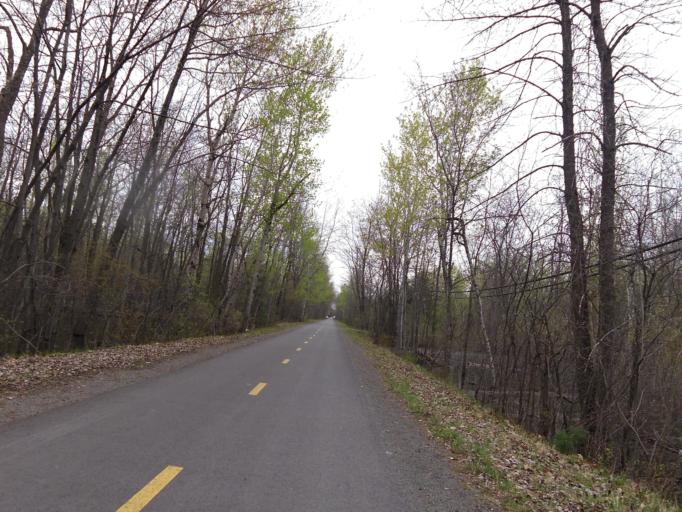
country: CA
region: Quebec
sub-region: Laurentides
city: Sainte-Marthe-sur-le-Lac
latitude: 45.5178
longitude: -73.9533
